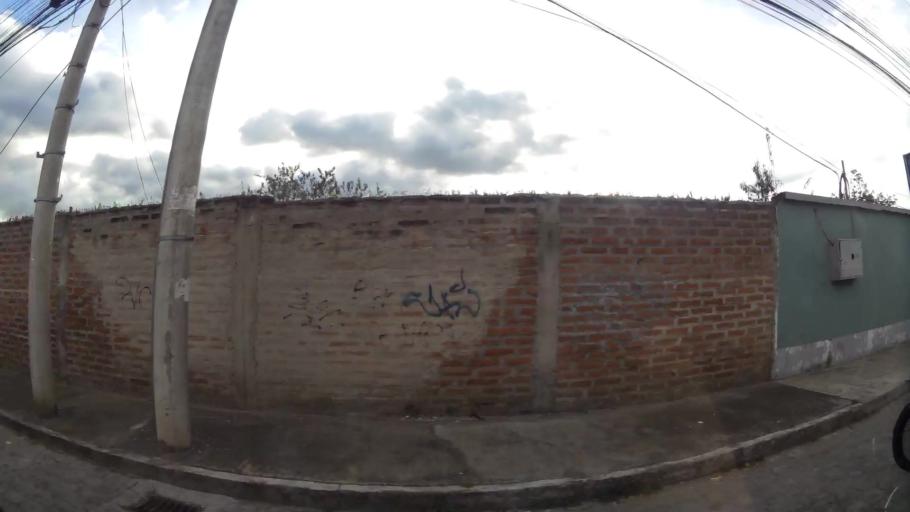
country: EC
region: Pichincha
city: Quito
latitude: -0.1461
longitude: -78.4711
